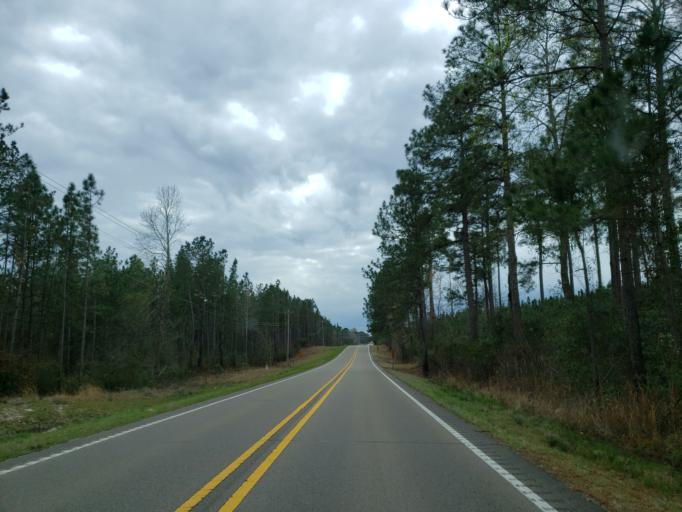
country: US
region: Mississippi
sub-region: Lamar County
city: Purvis
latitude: 31.2202
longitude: -89.3569
